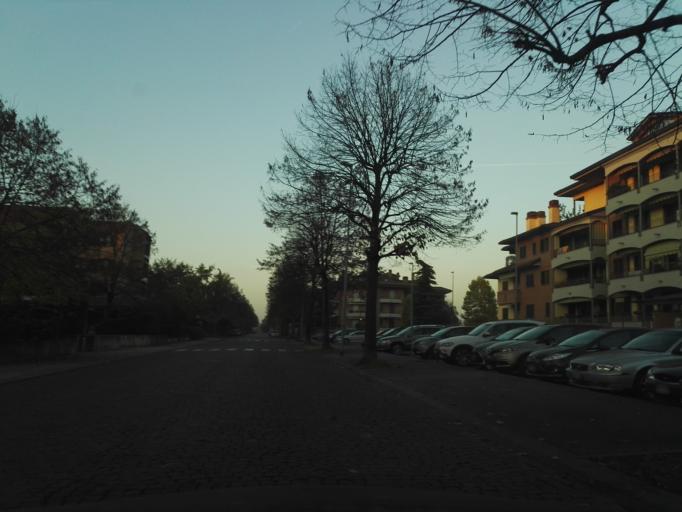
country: IT
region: Lombardy
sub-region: Citta metropolitana di Milano
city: Bettola-Zeloforomagno
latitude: 45.4337
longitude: 9.3161
